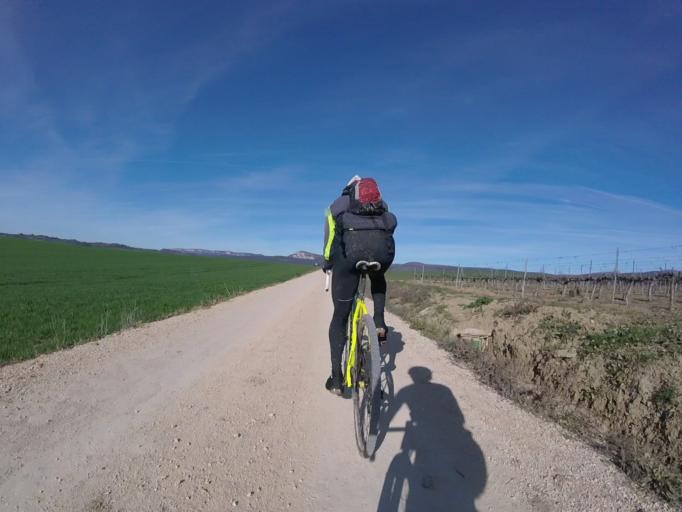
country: ES
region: Navarre
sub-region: Provincia de Navarra
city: Yerri
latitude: 42.7148
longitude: -1.9757
